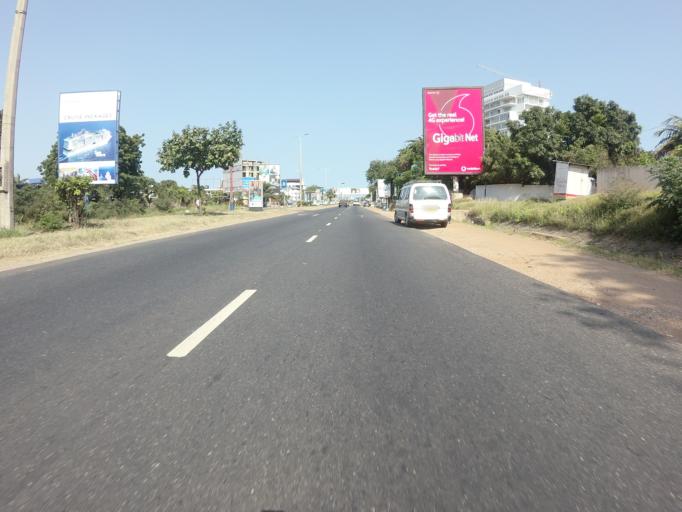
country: GH
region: Greater Accra
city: Accra
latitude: 5.5678
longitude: -0.1825
